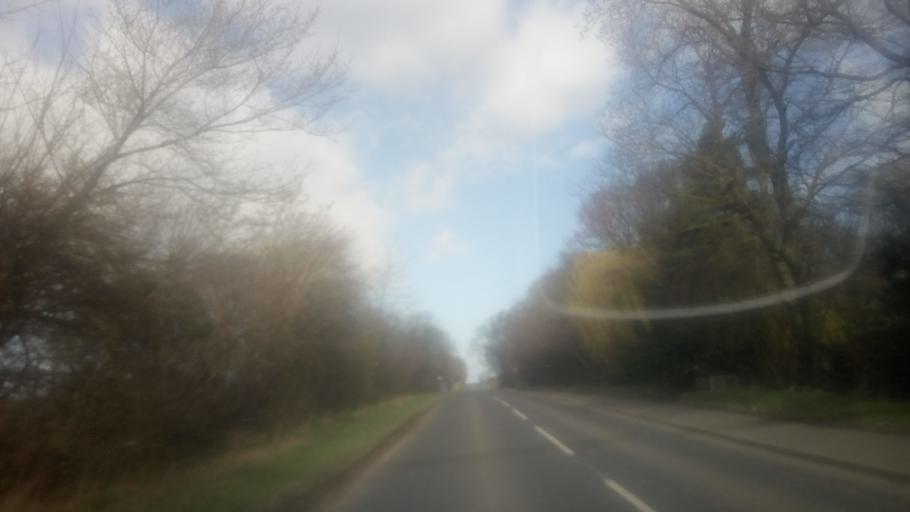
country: GB
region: Scotland
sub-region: East Lothian
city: Ormiston
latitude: 55.9191
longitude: -2.9352
